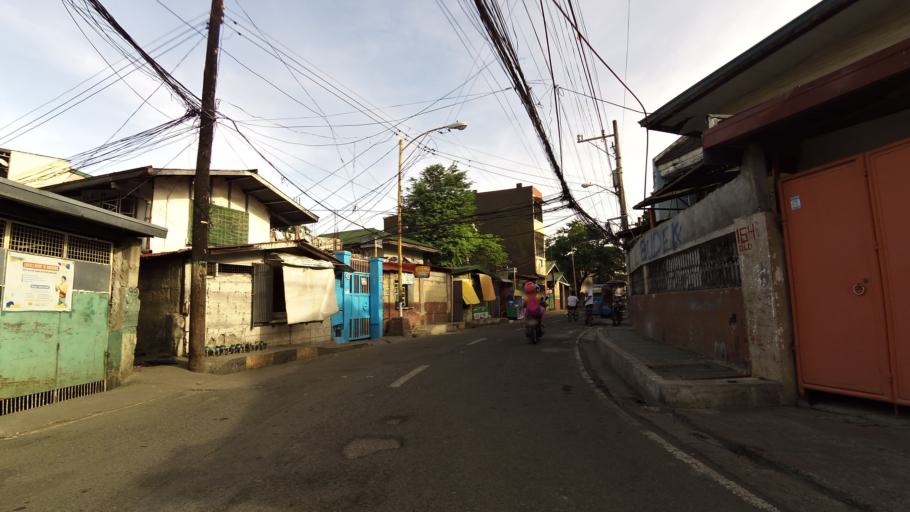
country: PH
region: Calabarzon
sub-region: Province of Rizal
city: Pateros
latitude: 14.5657
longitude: 121.0835
